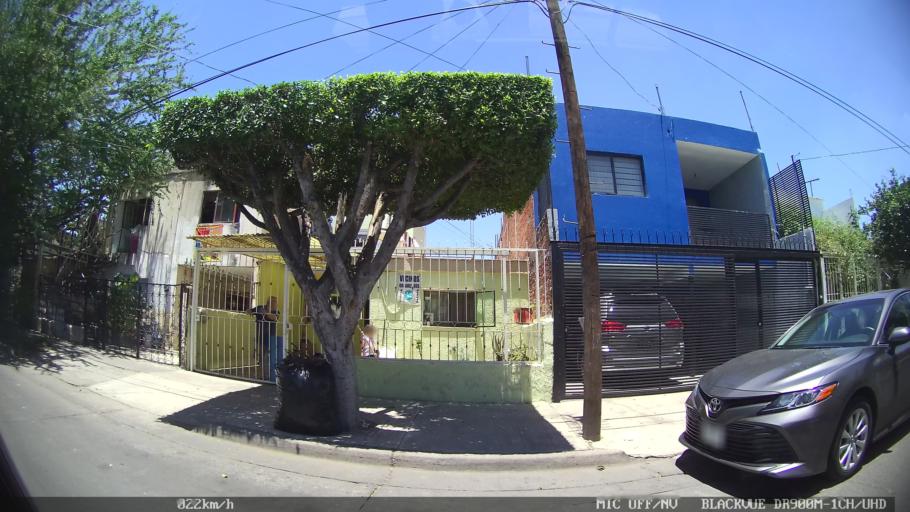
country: MX
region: Jalisco
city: Tlaquepaque
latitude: 20.6605
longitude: -103.2815
